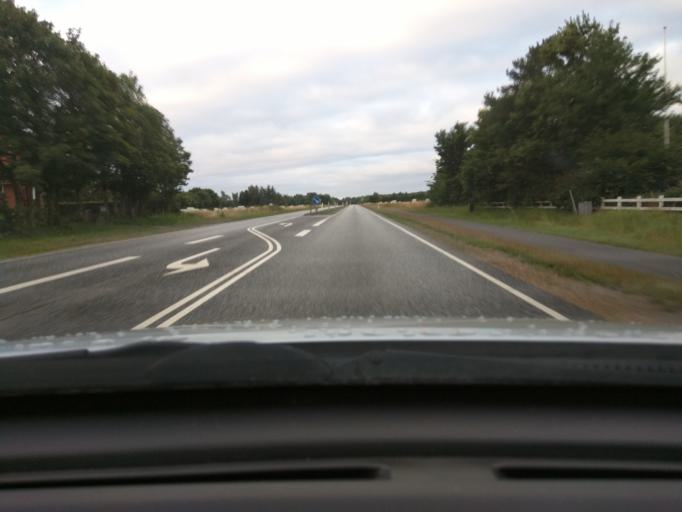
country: DK
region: Central Jutland
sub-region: Viborg Kommune
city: Viborg
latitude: 56.4136
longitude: 9.3775
